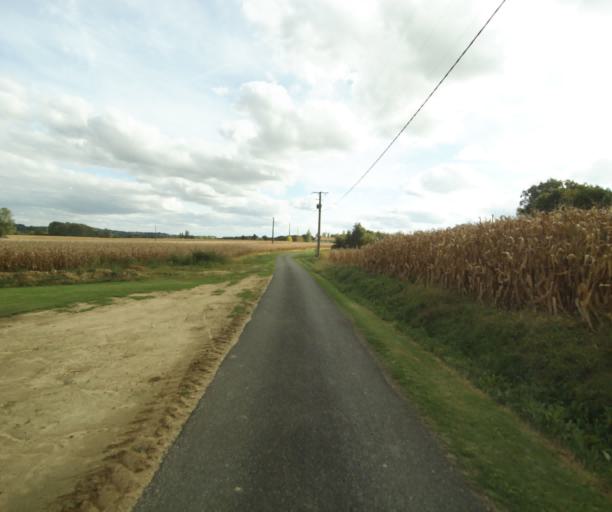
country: FR
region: Midi-Pyrenees
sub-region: Departement du Gers
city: Gondrin
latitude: 43.8540
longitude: 0.2240
